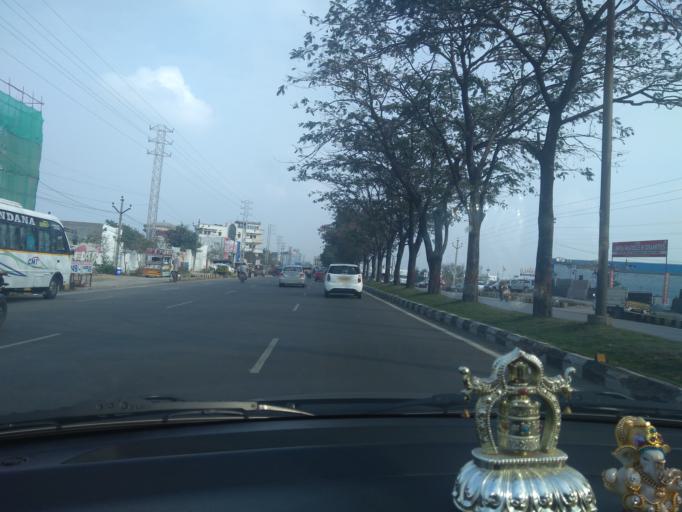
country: IN
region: Telangana
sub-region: Rangareddi
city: Balapur
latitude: 17.3160
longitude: 78.4412
